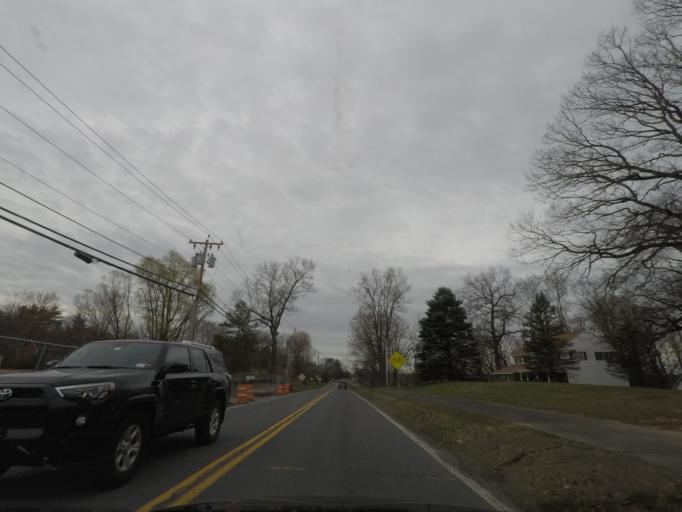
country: US
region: New York
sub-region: Albany County
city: Delmar
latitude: 42.6014
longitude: -73.8125
